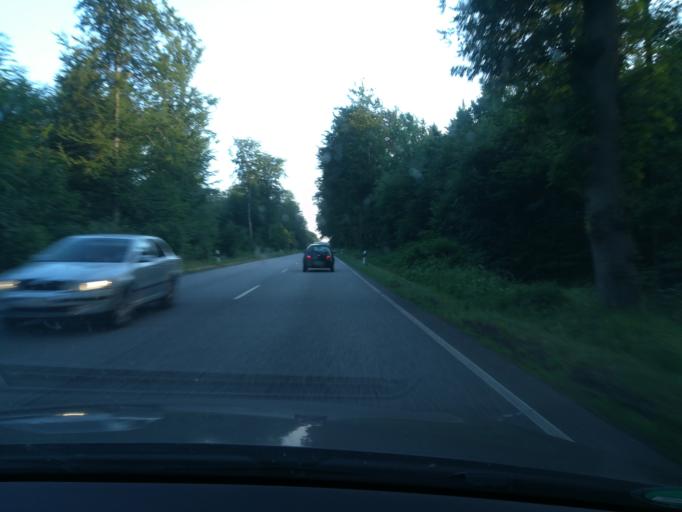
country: DE
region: Schleswig-Holstein
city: Kasseburg
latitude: 53.5444
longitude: 10.4205
